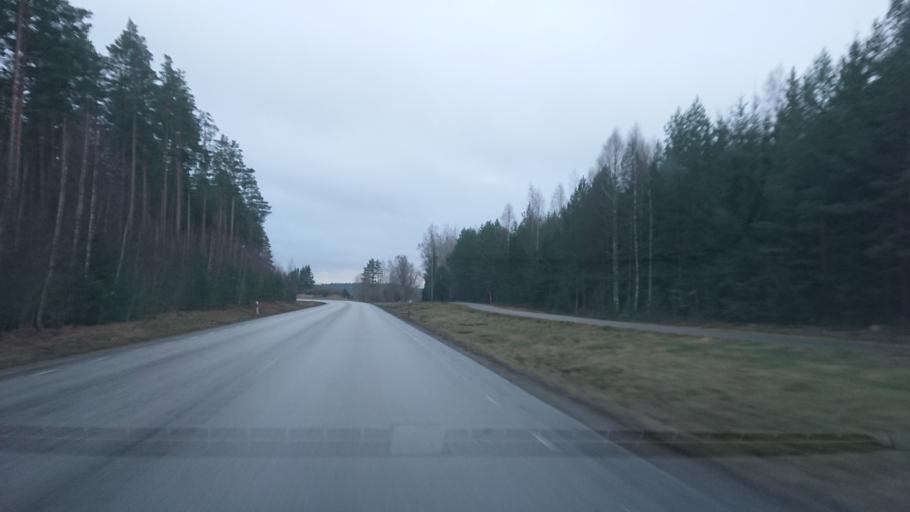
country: SE
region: Uppsala
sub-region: Osthammars Kommun
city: Bjorklinge
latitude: 60.0152
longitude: 17.5863
